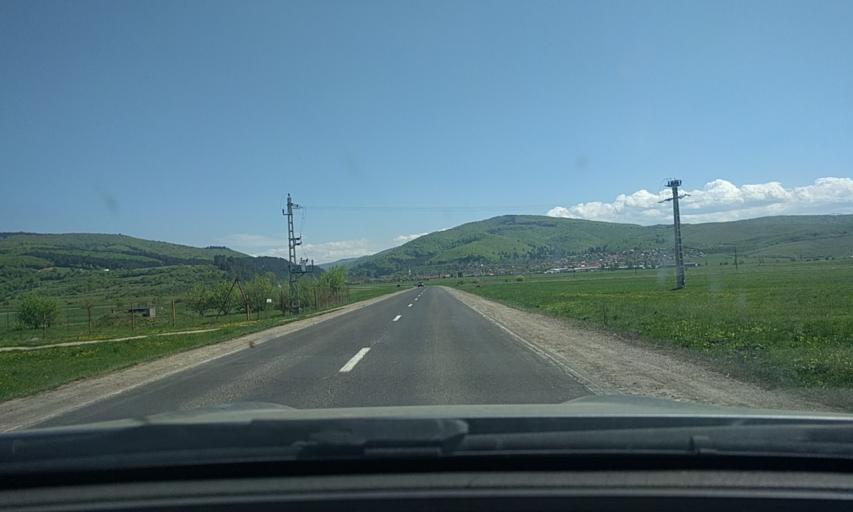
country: RO
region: Brasov
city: Tunelu-Teliu
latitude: 45.7096
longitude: 25.8305
